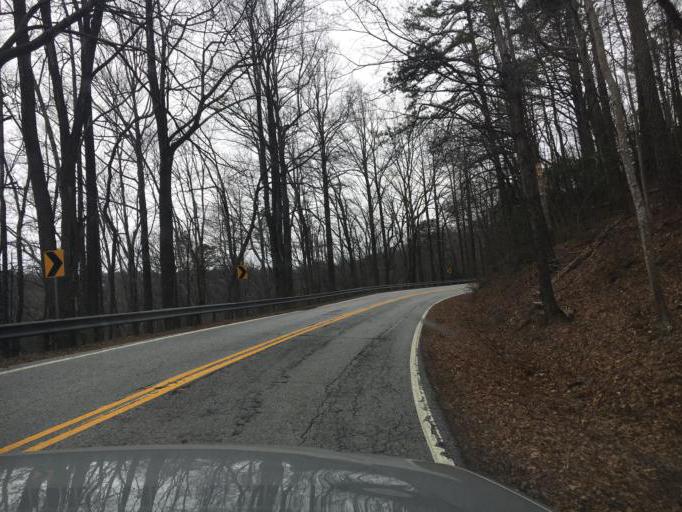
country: US
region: South Carolina
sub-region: Greenville County
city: Slater-Marietta
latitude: 35.1070
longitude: -82.6088
